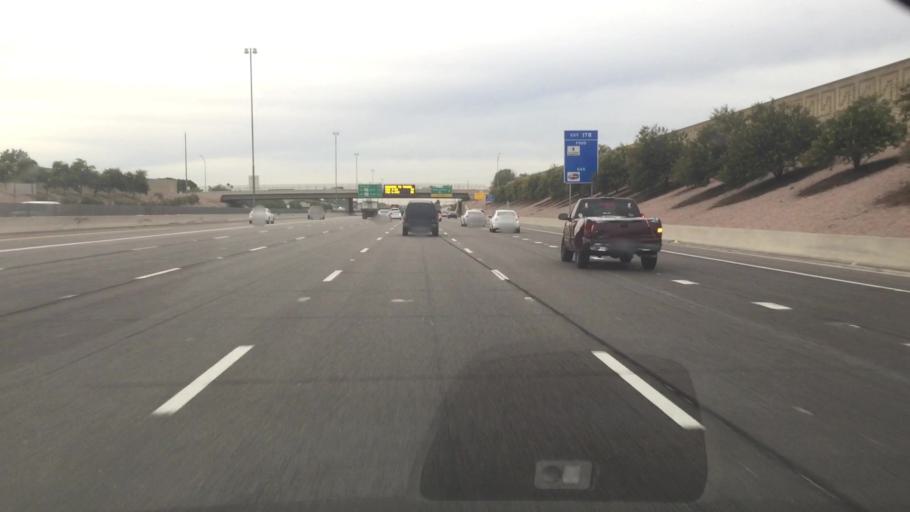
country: US
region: Arizona
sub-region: Maricopa County
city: San Carlos
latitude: 33.3864
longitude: -111.8461
